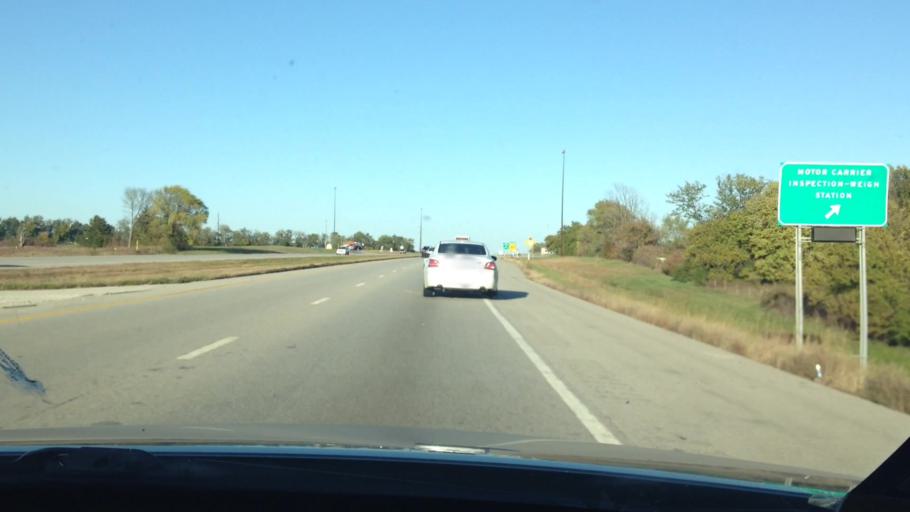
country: US
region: Kansas
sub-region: Johnson County
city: Olathe
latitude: 38.8290
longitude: -94.8548
